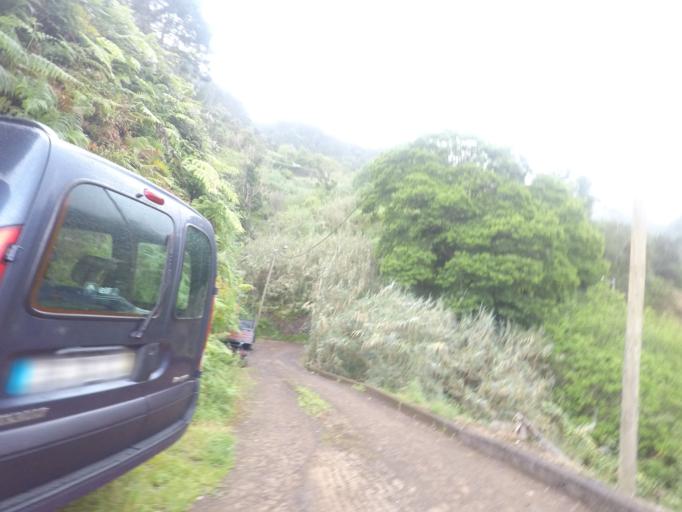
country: PT
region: Madeira
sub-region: Santana
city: Santana
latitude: 32.7703
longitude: -16.8767
